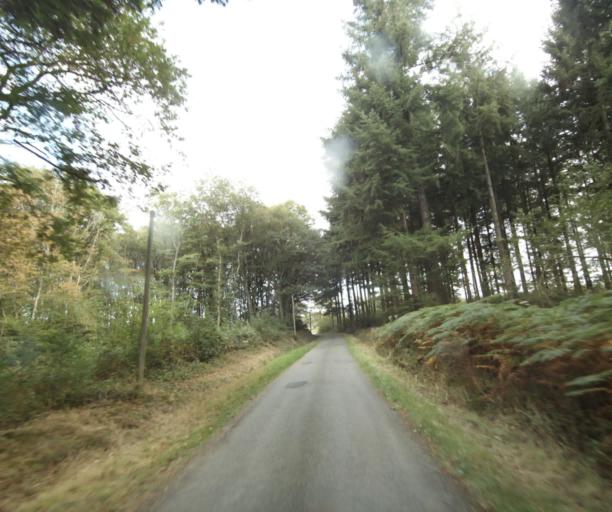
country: FR
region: Bourgogne
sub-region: Departement de Saone-et-Loire
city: Palinges
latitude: 46.5126
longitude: 4.2840
